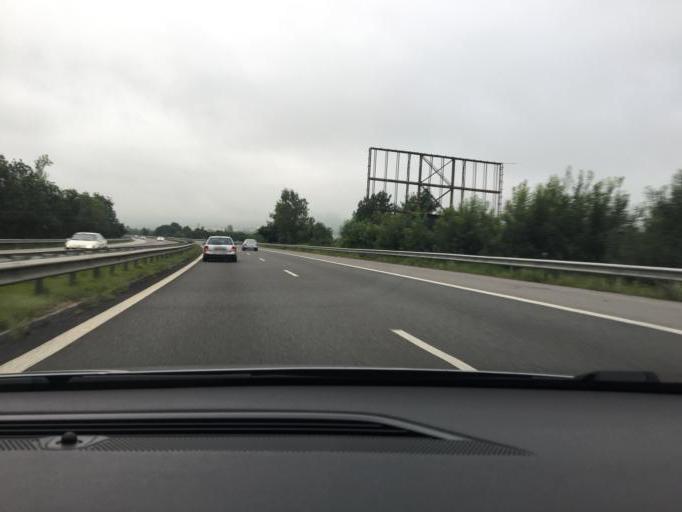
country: BG
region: Sofiya
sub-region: Obshtina Elin Pelin
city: Elin Pelin
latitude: 42.6169
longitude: 23.5252
